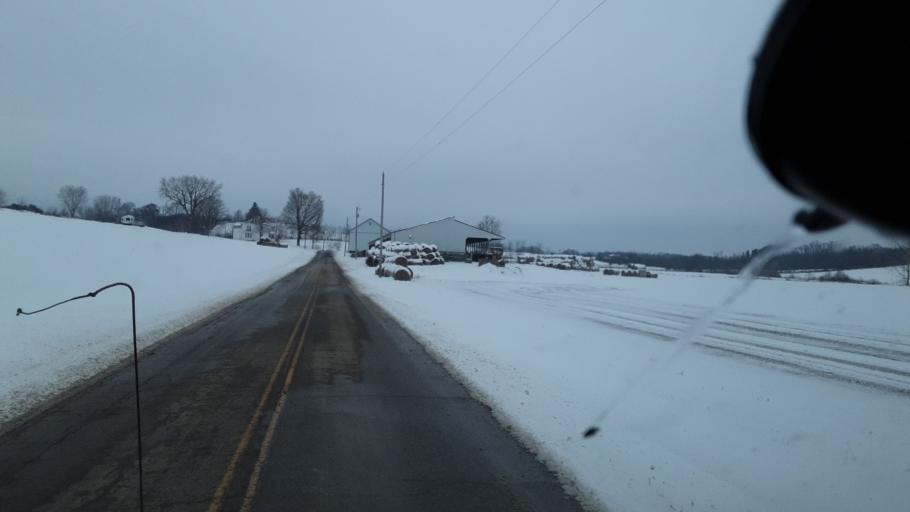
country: US
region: Ohio
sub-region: Perry County
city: Somerset
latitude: 39.9022
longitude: -82.2031
